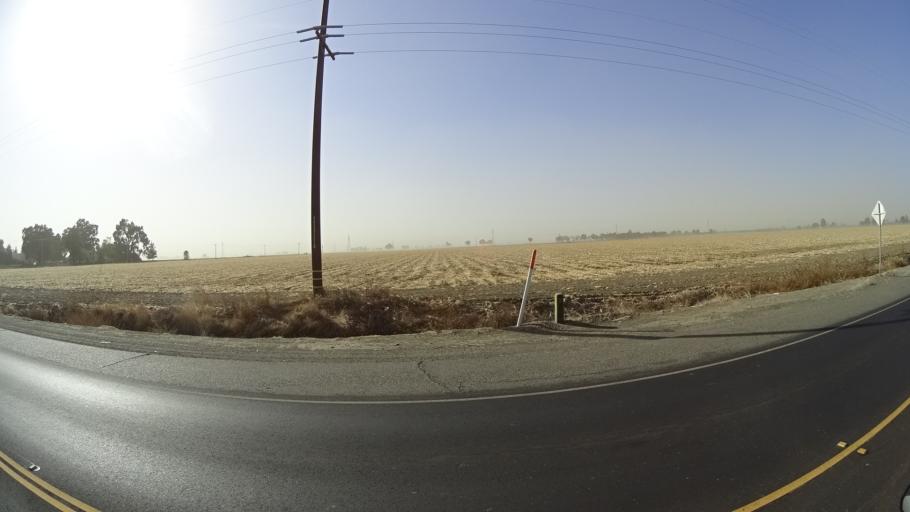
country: US
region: California
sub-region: Yolo County
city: Woodland
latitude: 38.7794
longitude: -121.7284
